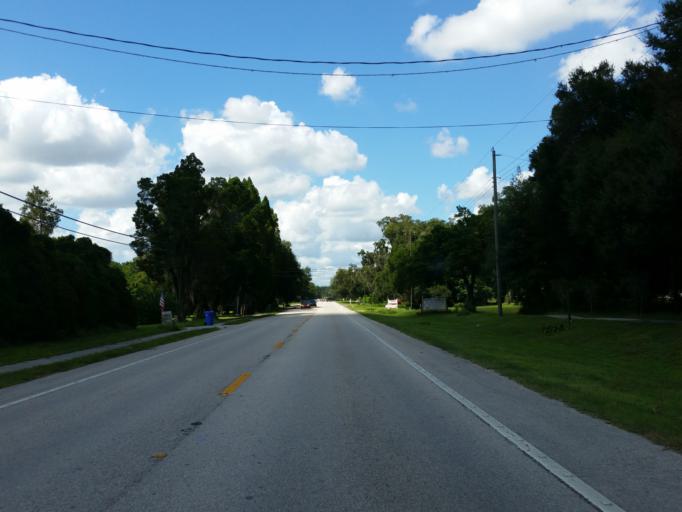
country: US
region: Florida
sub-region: Hillsborough County
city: Brandon
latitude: 27.9167
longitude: -82.2641
